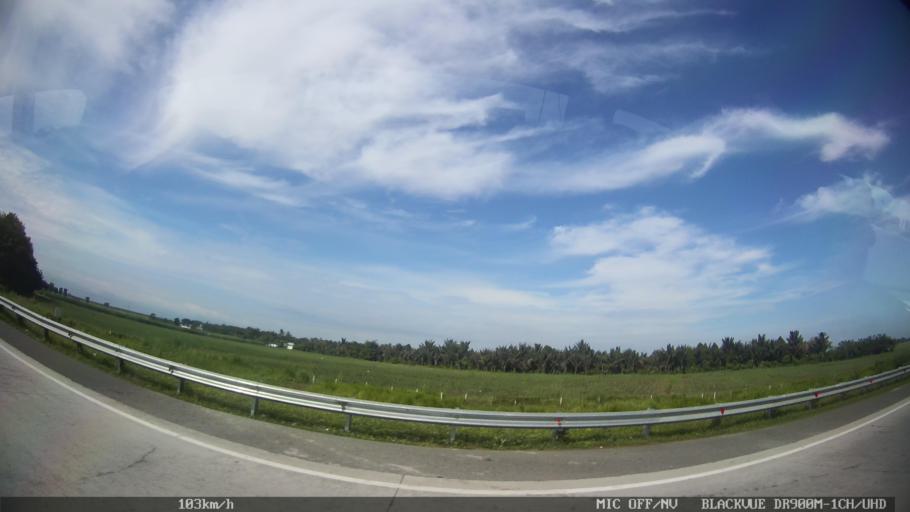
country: ID
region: North Sumatra
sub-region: Kabupaten Langkat
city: Stabat
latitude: 3.7026
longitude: 98.5390
